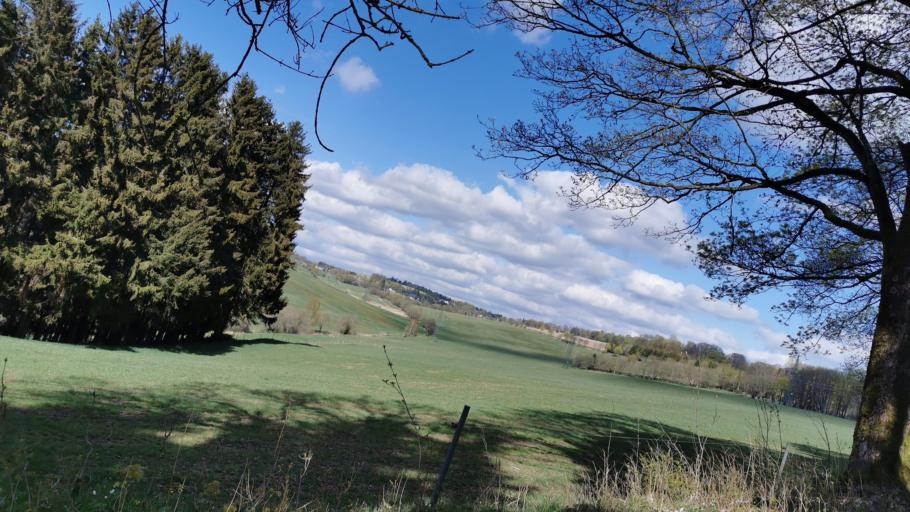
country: DE
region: Bavaria
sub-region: Upper Franconia
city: Ludwigsstadt
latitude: 50.4680
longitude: 11.4234
